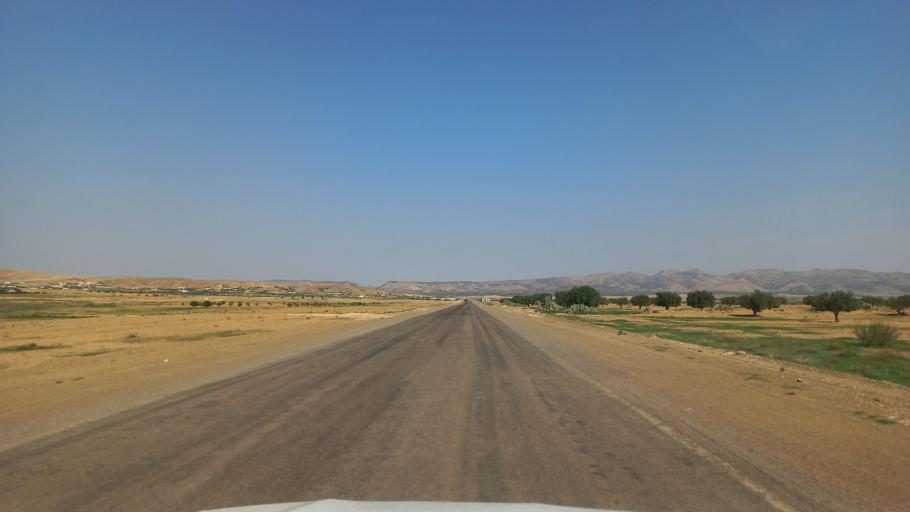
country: TN
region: Al Qasrayn
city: Sbiba
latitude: 35.3676
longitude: 9.0394
